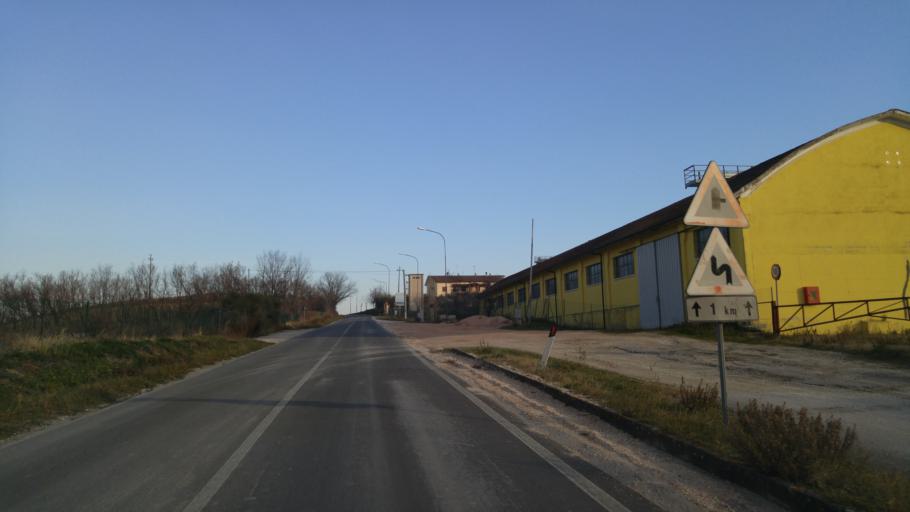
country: IT
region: The Marches
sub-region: Provincia di Pesaro e Urbino
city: San Giorgio di Pesaro
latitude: 43.7100
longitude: 12.9961
